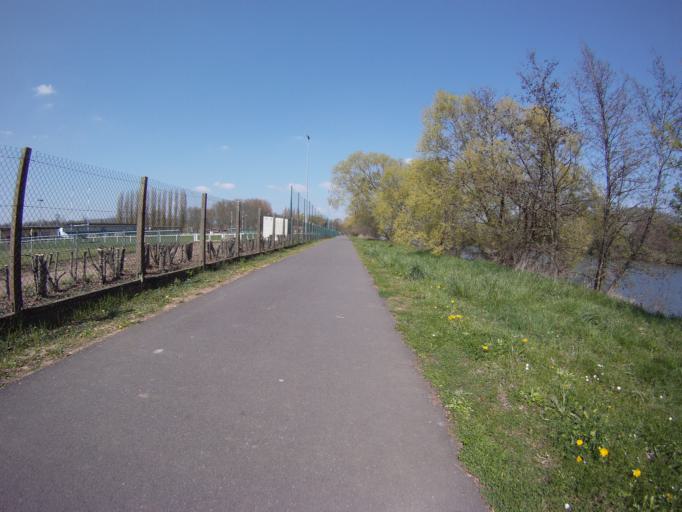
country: FR
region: Lorraine
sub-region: Departement de Meurthe-et-Moselle
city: Pont-a-Mousson
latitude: 48.8948
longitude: 6.0600
